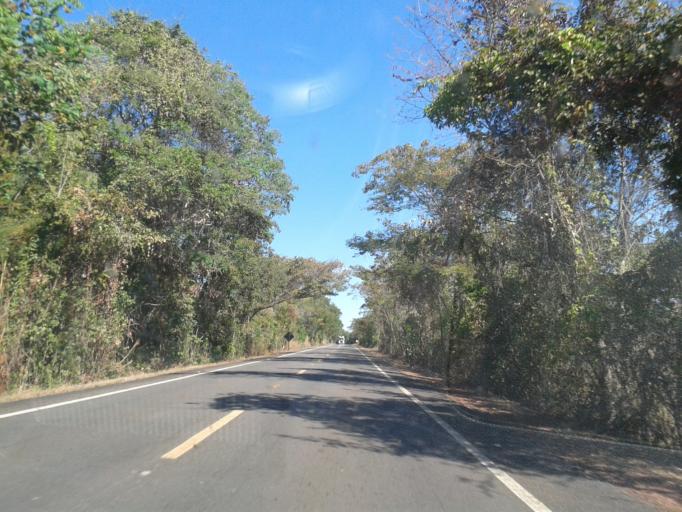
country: BR
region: Goias
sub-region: Sao Miguel Do Araguaia
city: Sao Miguel do Araguaia
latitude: -13.8076
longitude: -50.3426
